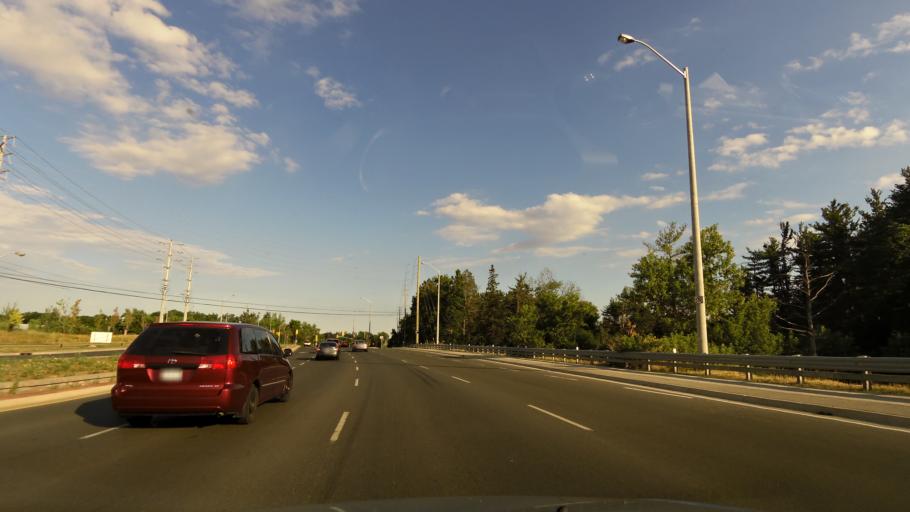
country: CA
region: Ontario
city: Brampton
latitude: 43.6487
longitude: -79.8048
